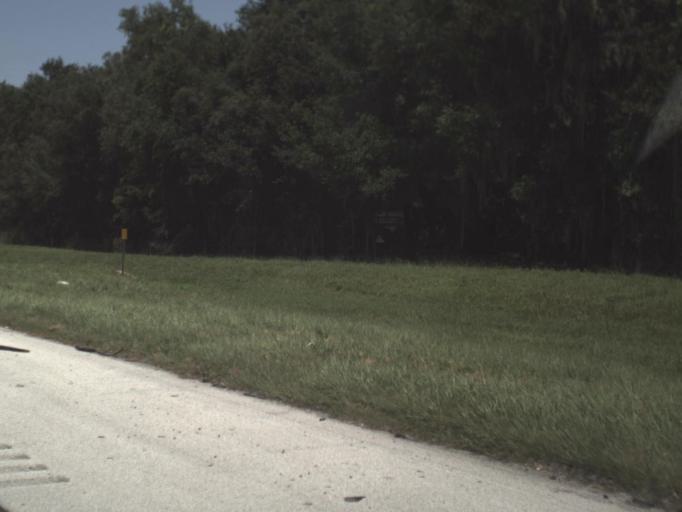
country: US
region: Florida
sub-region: Hillsborough County
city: Dover
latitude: 28.0278
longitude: -82.2164
